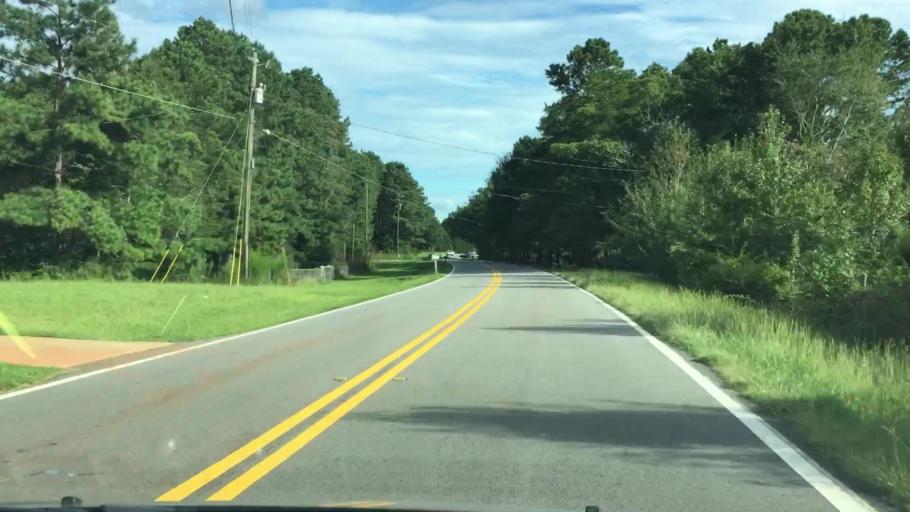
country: US
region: Georgia
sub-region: Clayton County
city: Conley
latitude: 33.6405
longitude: -84.2614
